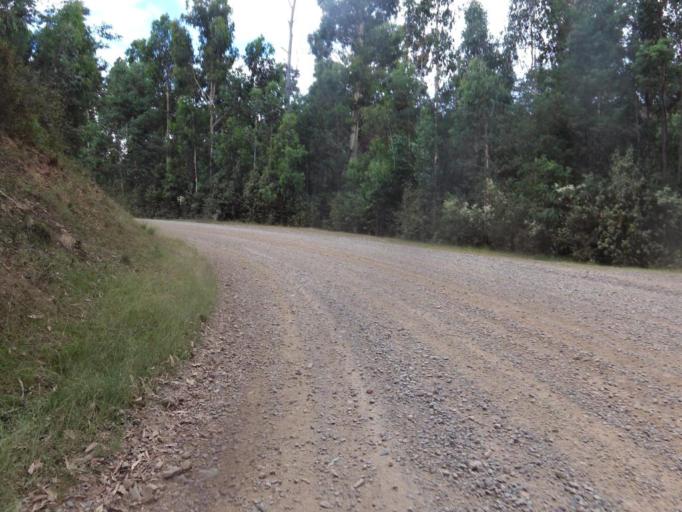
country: AU
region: Victoria
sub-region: Yarra Ranges
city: Healesville
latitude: -37.4016
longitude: 145.5608
